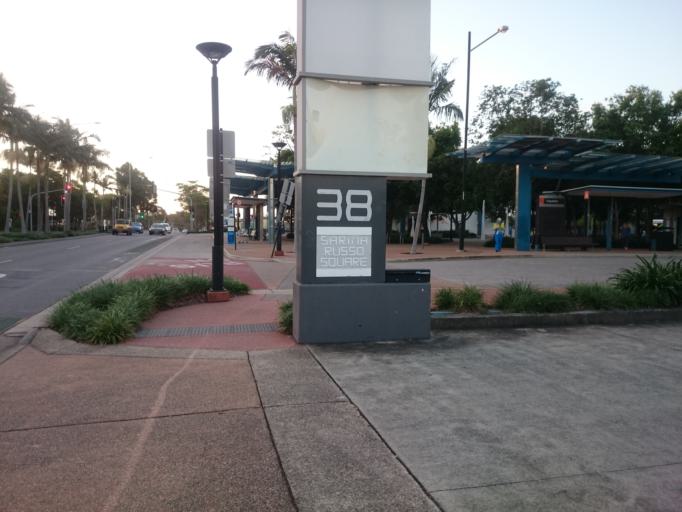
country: AU
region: Queensland
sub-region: Brisbane
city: Chandler
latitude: -27.5238
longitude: 153.1922
